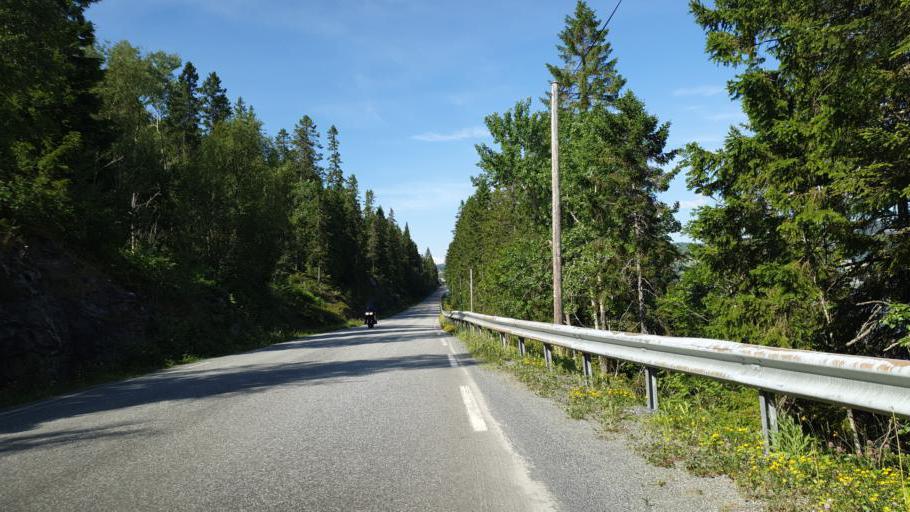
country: NO
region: Nord-Trondelag
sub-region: Leksvik
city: Leksvik
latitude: 63.6516
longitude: 10.6084
